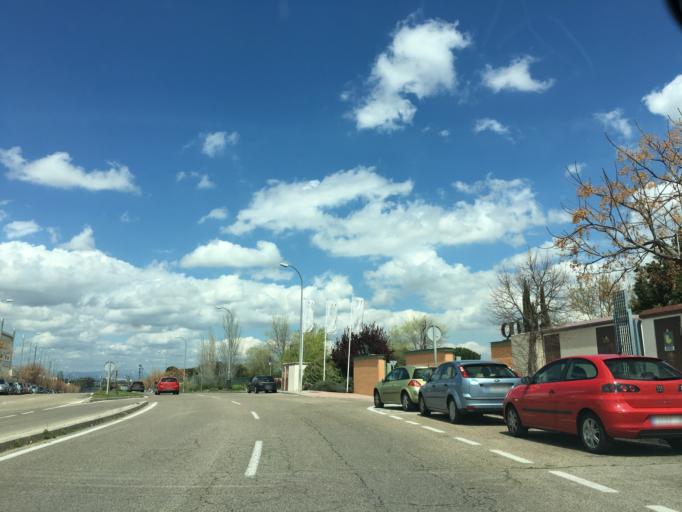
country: ES
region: Madrid
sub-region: Provincia de Madrid
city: San Blas
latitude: 40.4652
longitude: -3.6115
